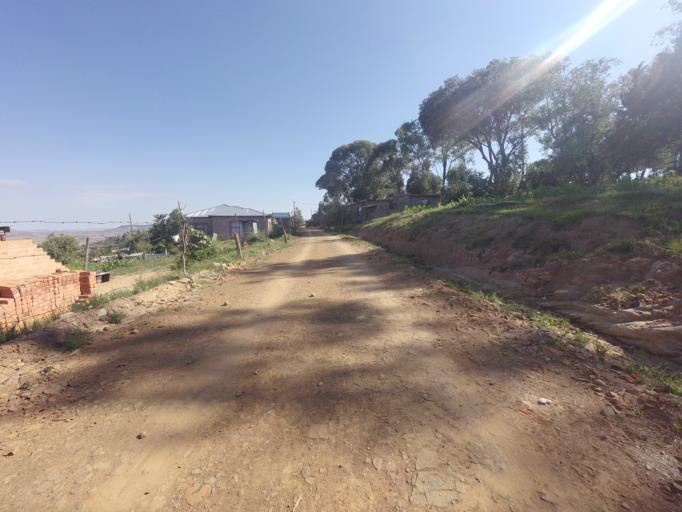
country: LS
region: Berea
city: Teyateyaneng
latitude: -29.1443
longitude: 27.7478
